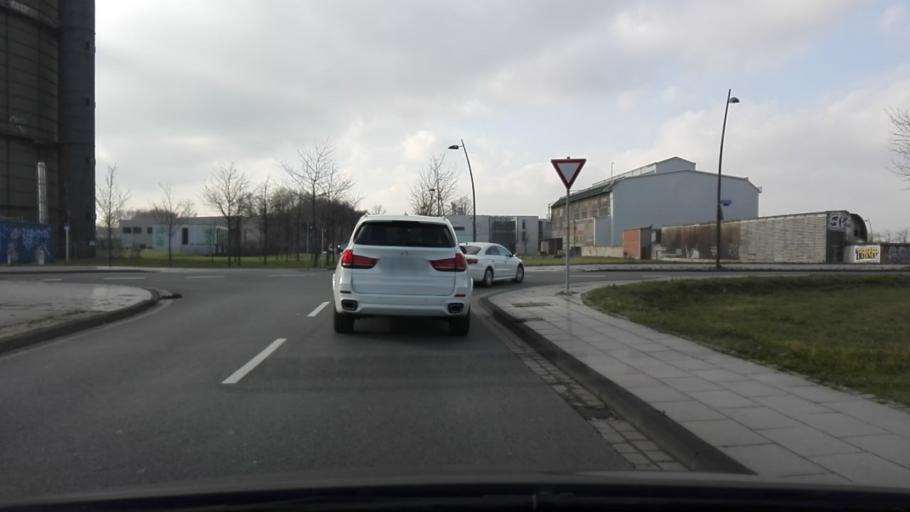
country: DE
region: North Rhine-Westphalia
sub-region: Regierungsbezirk Arnsberg
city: Dortmund
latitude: 51.4857
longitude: 7.4864
